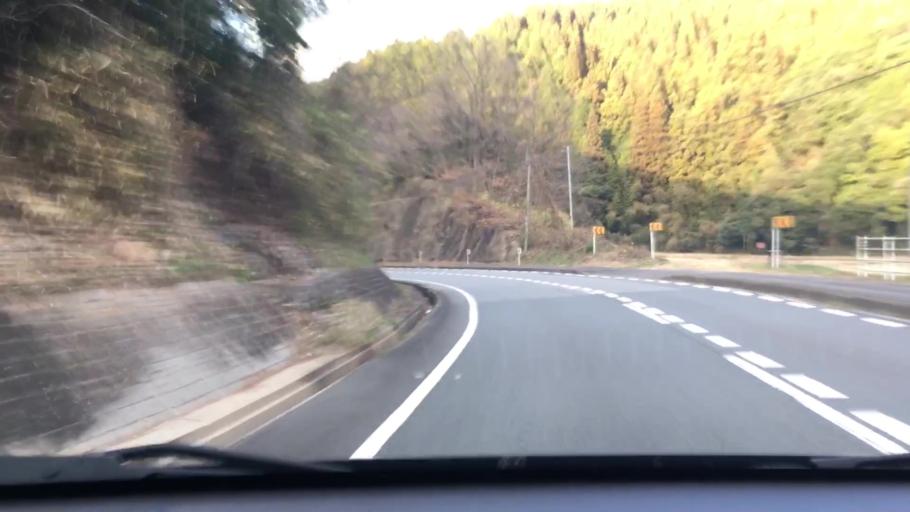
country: JP
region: Oita
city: Hiji
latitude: 33.4250
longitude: 131.4138
